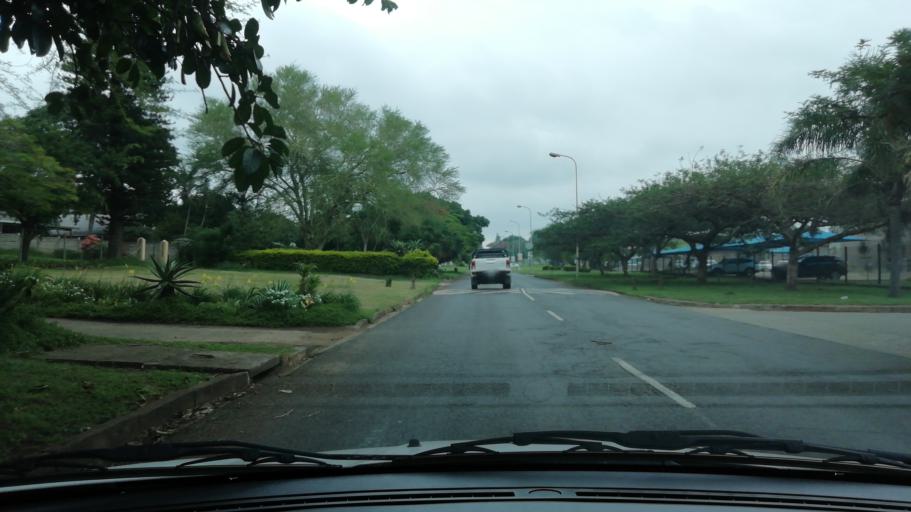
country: ZA
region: KwaZulu-Natal
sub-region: uThungulu District Municipality
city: Empangeni
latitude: -28.7355
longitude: 31.8948
